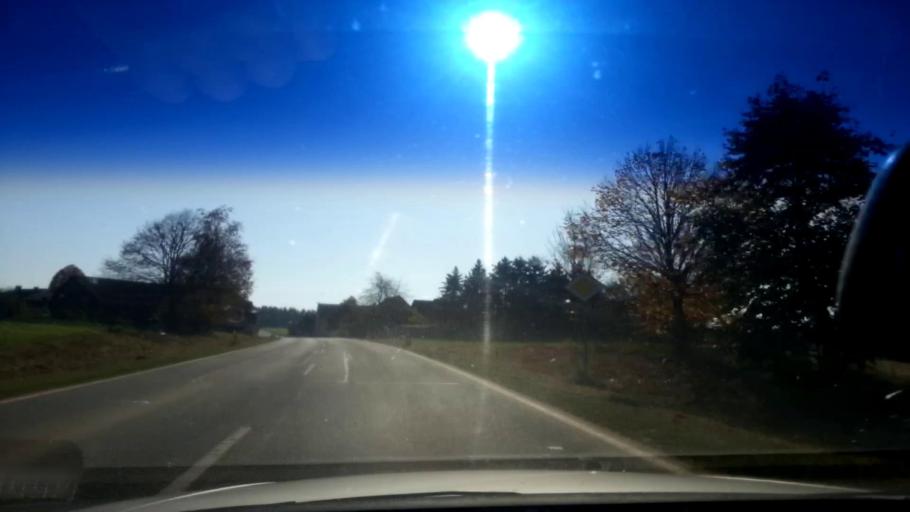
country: DE
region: Bavaria
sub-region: Upper Franconia
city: Stadelhofen
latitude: 49.9878
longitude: 11.2277
